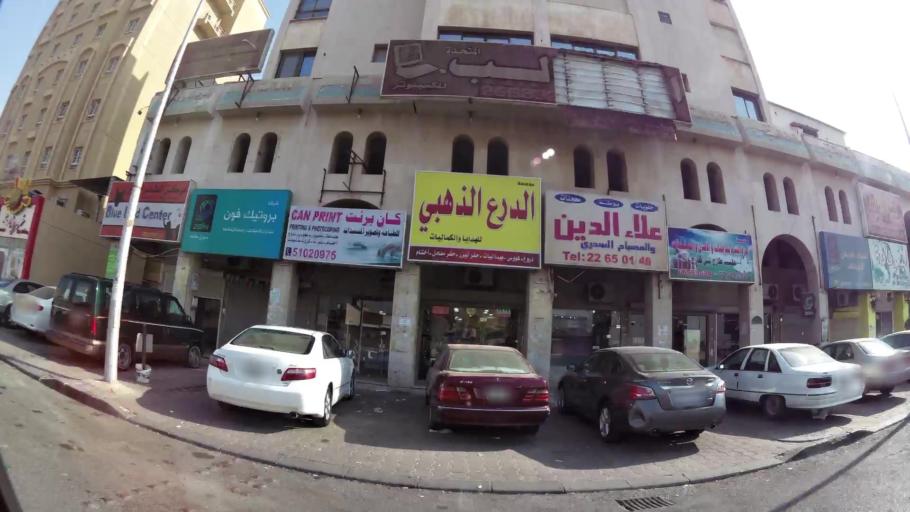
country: KW
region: Muhafazat Hawalli
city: Hawalli
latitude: 29.3259
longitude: 48.0137
